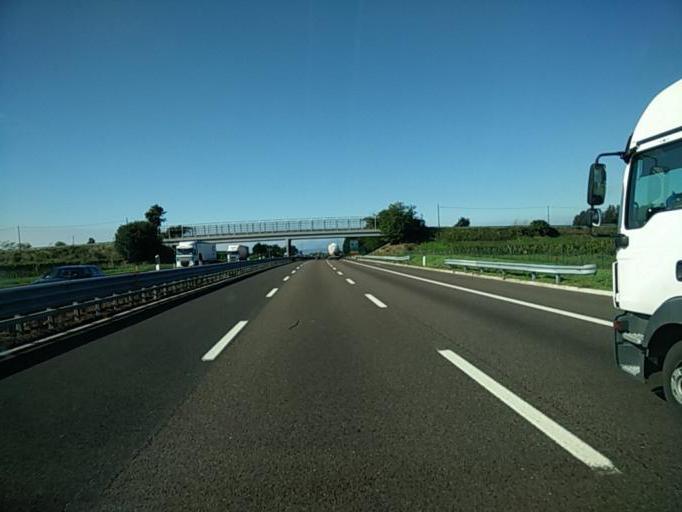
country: IT
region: Veneto
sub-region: Provincia di Verona
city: San Giorgio in Salici
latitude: 45.4210
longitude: 10.7828
